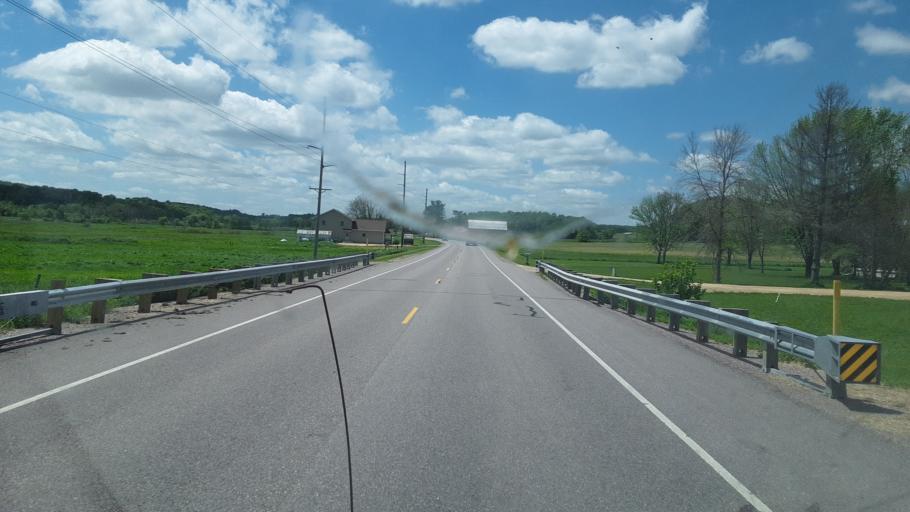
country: US
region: Wisconsin
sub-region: Sauk County
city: Reedsburg
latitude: 43.5935
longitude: -89.9231
